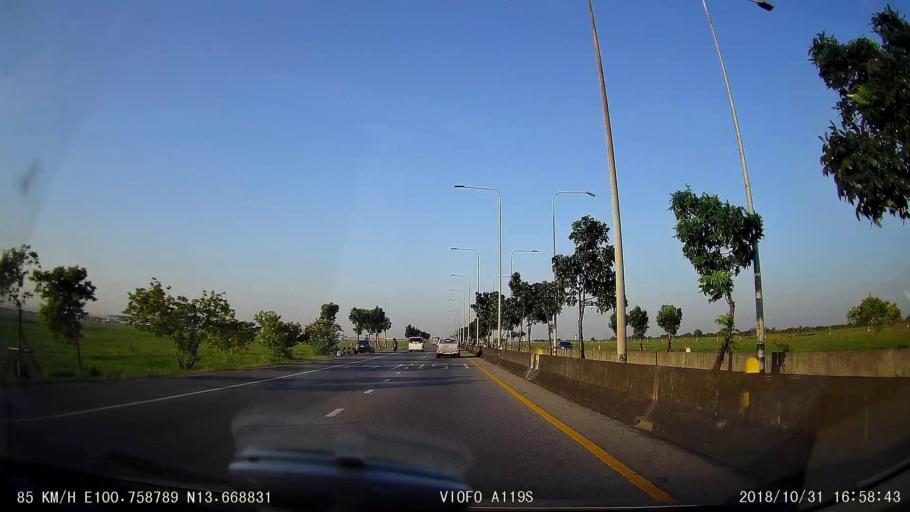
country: TH
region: Bangkok
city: Lat Krabang
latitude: 13.6691
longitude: 100.7589
